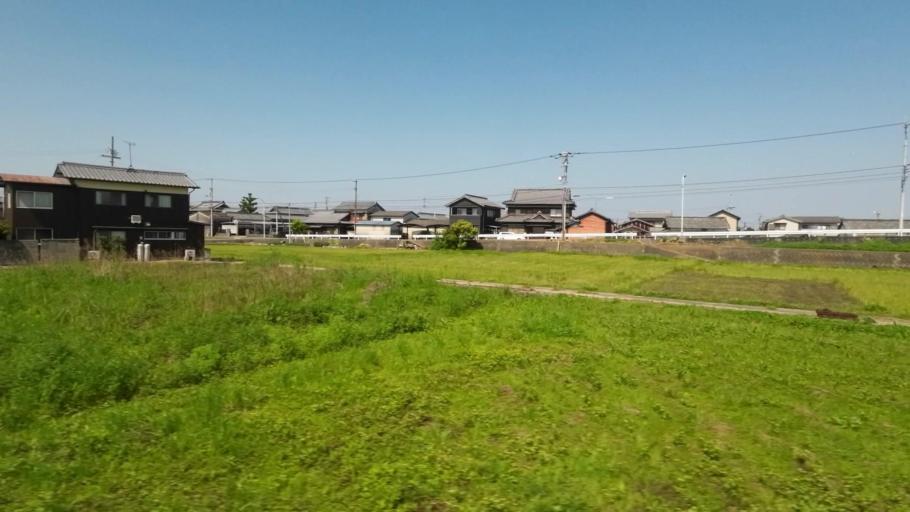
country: JP
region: Kagawa
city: Kan'onjicho
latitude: 34.1081
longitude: 133.6499
